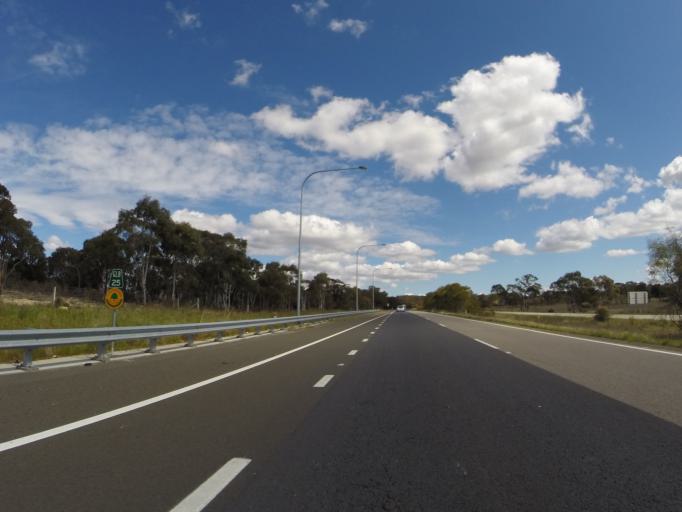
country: AU
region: New South Wales
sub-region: Goulburn Mulwaree
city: Goulburn
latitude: -34.7333
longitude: 149.9730
